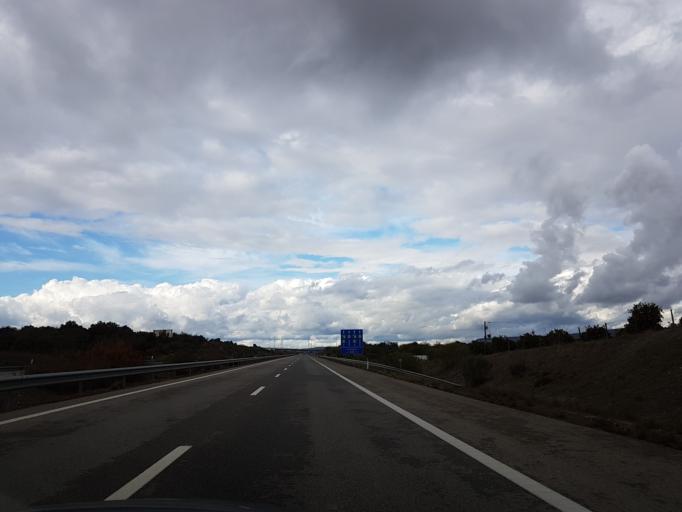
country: PT
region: Faro
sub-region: Albufeira
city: Ferreiras
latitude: 37.1880
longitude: -8.2197
